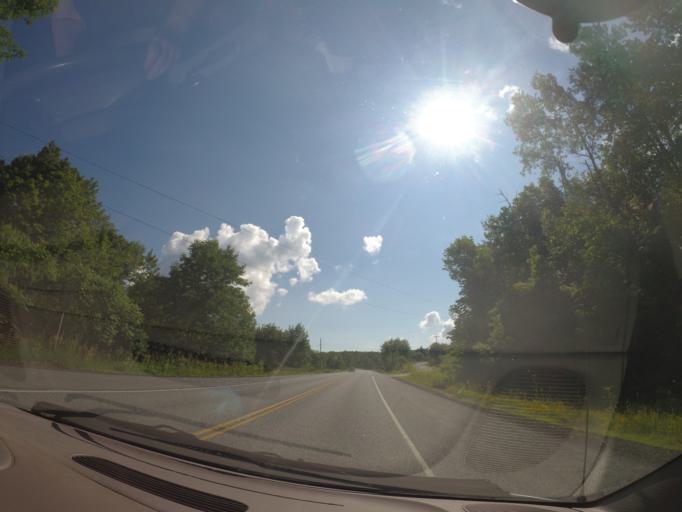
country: US
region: Vermont
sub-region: Bennington County
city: Bennington
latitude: 42.8922
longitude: -73.0029
